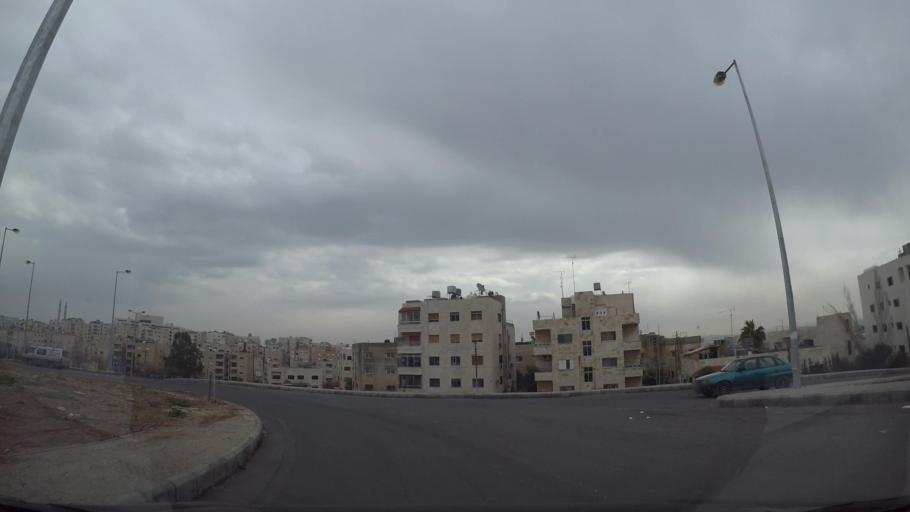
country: JO
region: Amman
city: Amman
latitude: 31.9812
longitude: 35.9309
